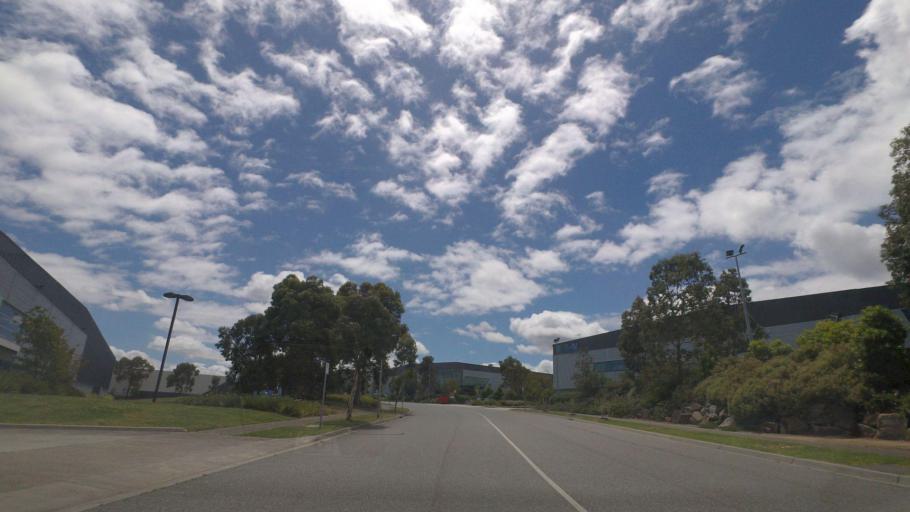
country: AU
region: Victoria
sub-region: Knox
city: Scoresby
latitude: -37.9082
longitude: 145.2419
